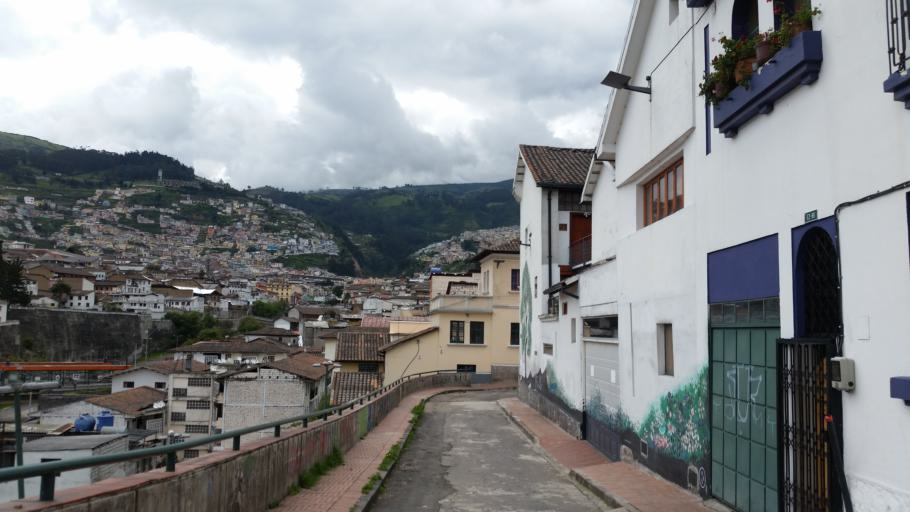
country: EC
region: Pichincha
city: Quito
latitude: -0.2269
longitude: -78.5114
